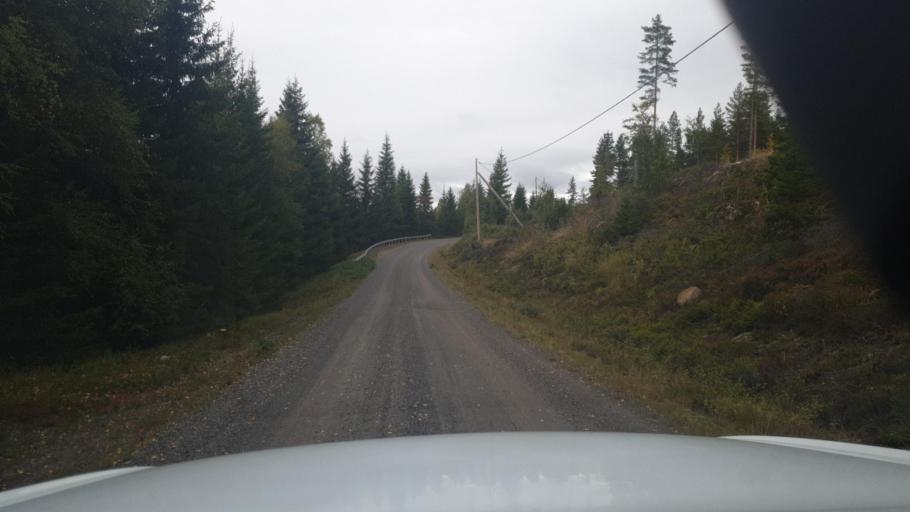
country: SE
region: Vaermland
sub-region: Eda Kommun
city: Charlottenberg
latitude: 60.1318
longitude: 12.5922
